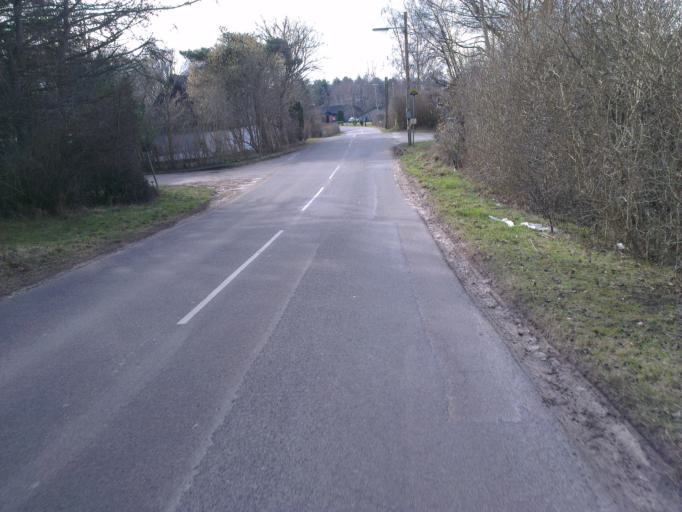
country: DK
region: Capital Region
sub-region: Halsnaes Kommune
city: Hundested
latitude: 55.9282
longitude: 11.9286
